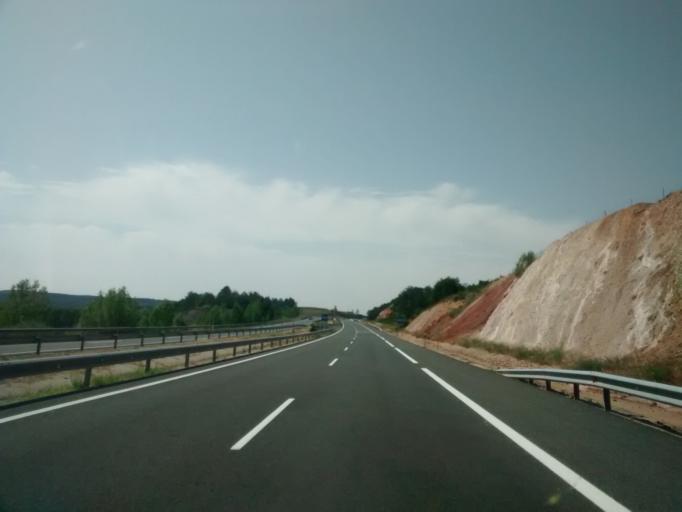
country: ES
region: Castille and Leon
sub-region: Provincia de Palencia
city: Aguilar de Campoo
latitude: 42.7361
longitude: -4.2893
